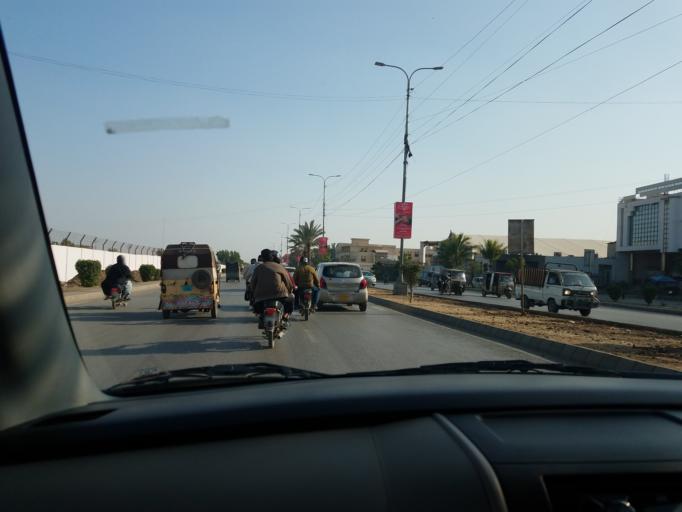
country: PK
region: Sindh
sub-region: Karachi District
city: Karachi
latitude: 24.8960
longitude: 67.1192
